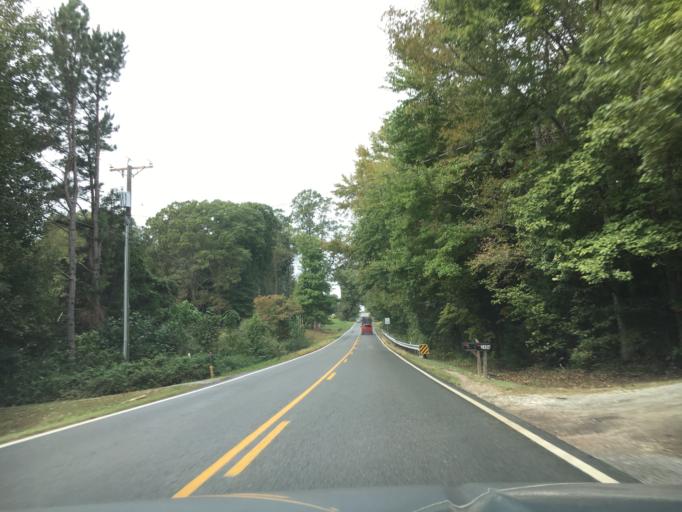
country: US
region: Virginia
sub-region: Goochland County
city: Goochland
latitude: 37.7455
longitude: -77.8521
